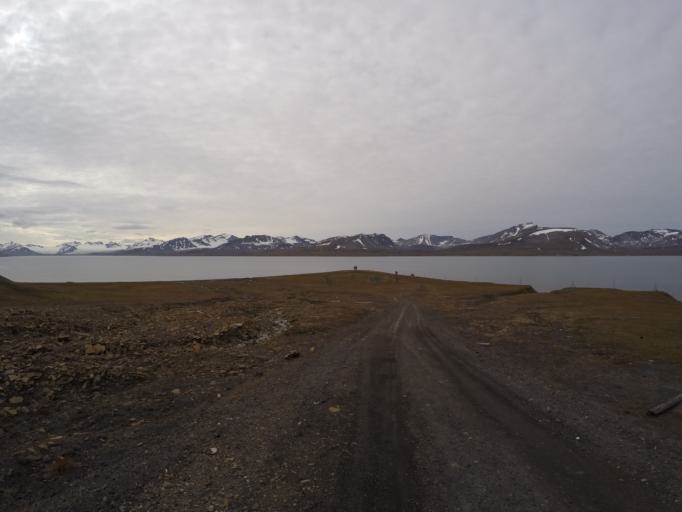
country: SJ
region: Svalbard
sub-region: Spitsbergen
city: Longyearbyen
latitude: 78.0458
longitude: 14.2263
